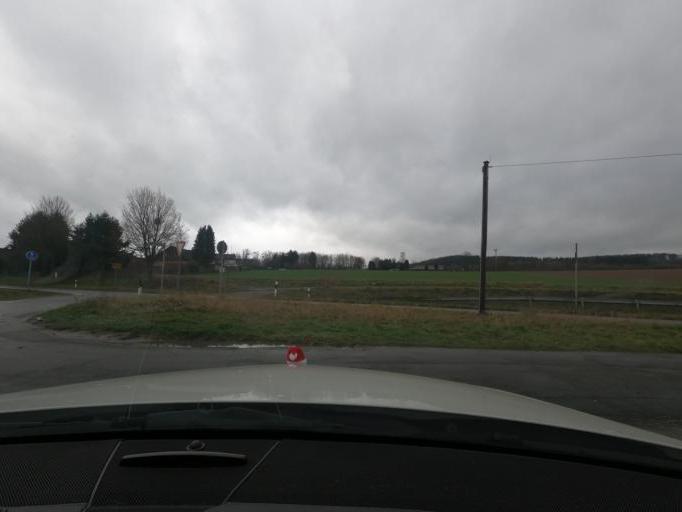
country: DE
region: Lower Saxony
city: Seesen
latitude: 51.8542
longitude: 10.1305
